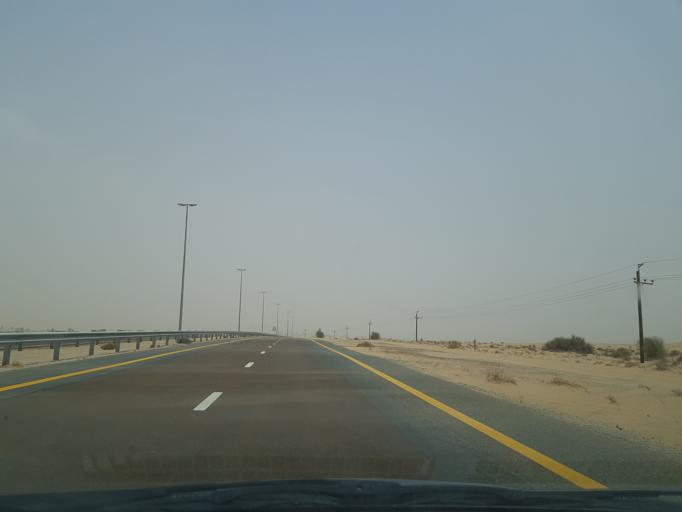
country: AE
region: Dubai
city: Dubai
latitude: 24.8876
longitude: 55.4245
